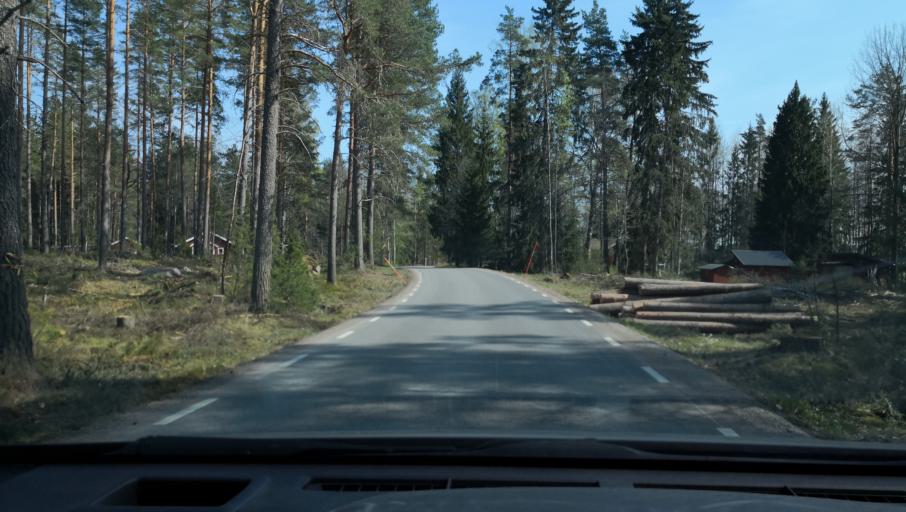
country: SE
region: Vaestmanland
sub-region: Sala Kommun
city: Sala
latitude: 60.0097
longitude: 16.6852
